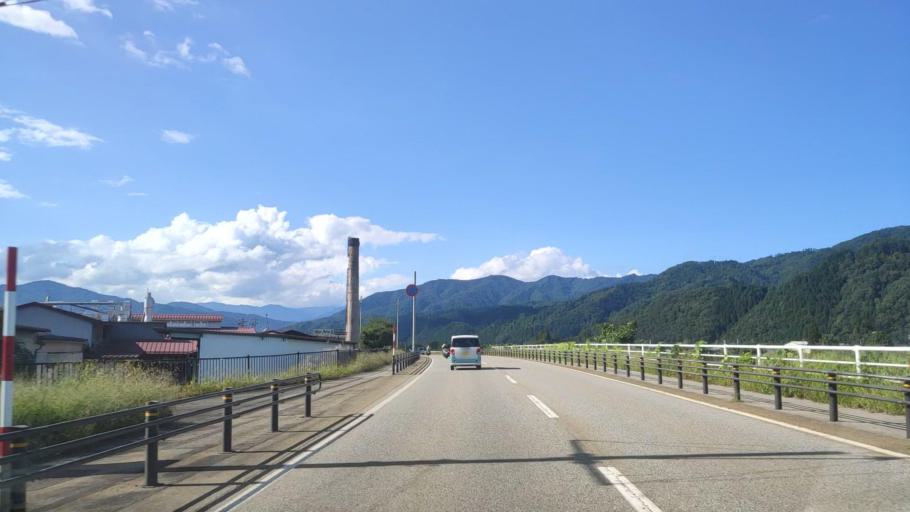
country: JP
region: Gifu
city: Takayama
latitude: 36.2420
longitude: 137.1730
